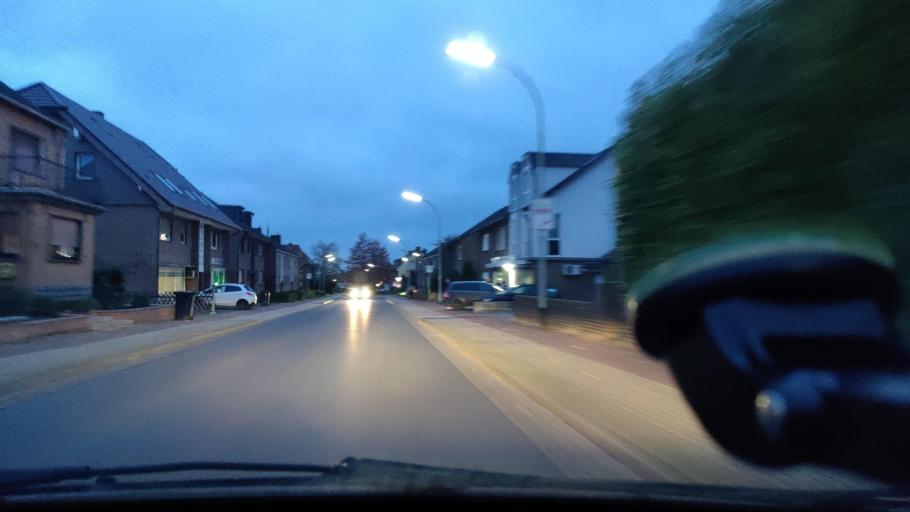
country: DE
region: North Rhine-Westphalia
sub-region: Regierungsbezirk Dusseldorf
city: Xanten
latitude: 51.6550
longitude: 6.4578
